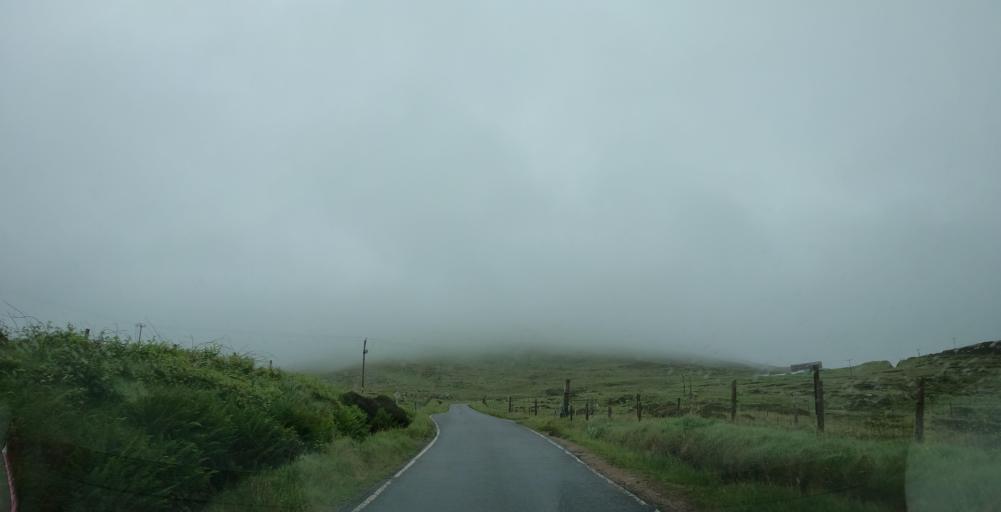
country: GB
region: Scotland
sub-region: Eilean Siar
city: Barra
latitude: 56.9585
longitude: -7.4705
